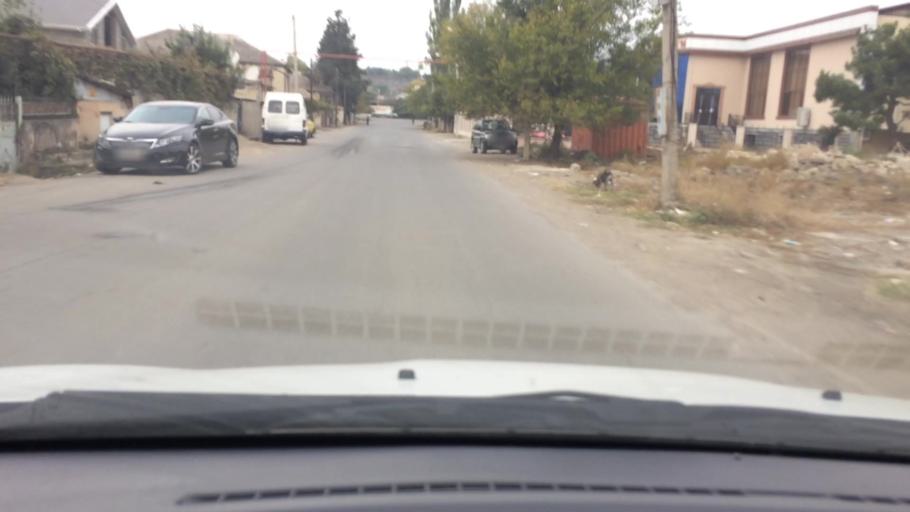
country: GE
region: Kvemo Kartli
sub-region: Marneuli
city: Marneuli
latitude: 41.4821
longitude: 44.7949
